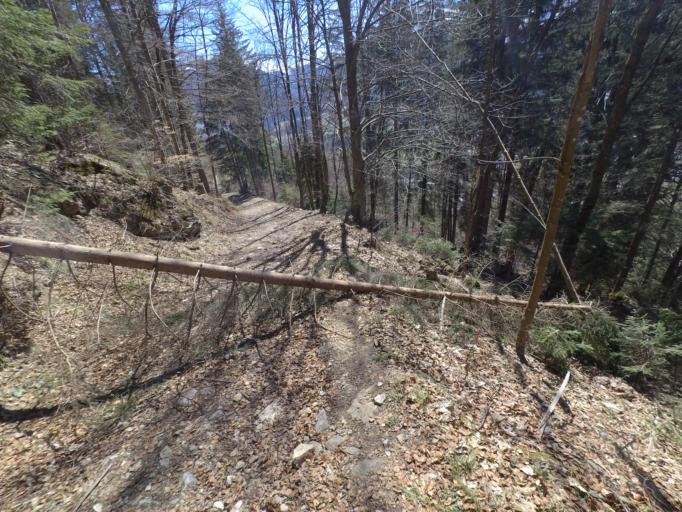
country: AT
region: Salzburg
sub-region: Politischer Bezirk Sankt Johann im Pongau
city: Sankt Veit im Pongau
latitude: 47.3357
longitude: 13.1596
